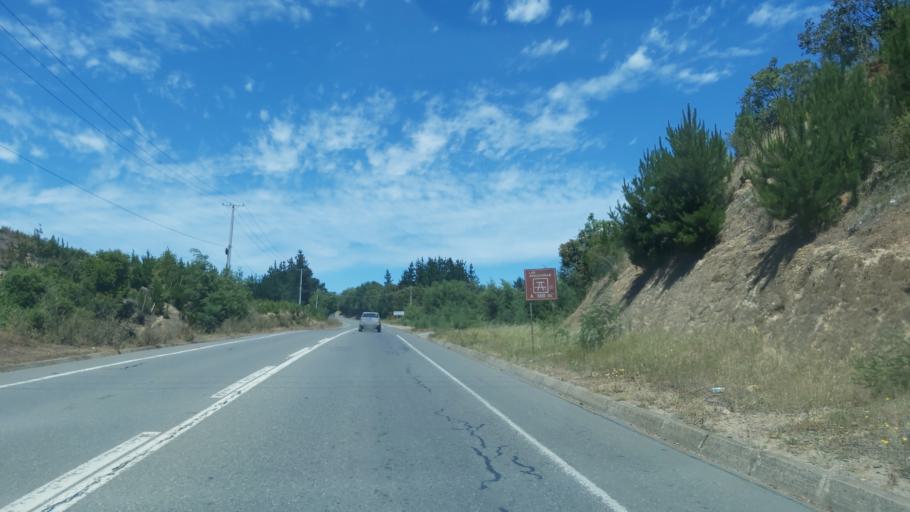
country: CL
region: Maule
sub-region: Provincia de Talca
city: Constitucion
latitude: -35.3232
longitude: -72.3854
